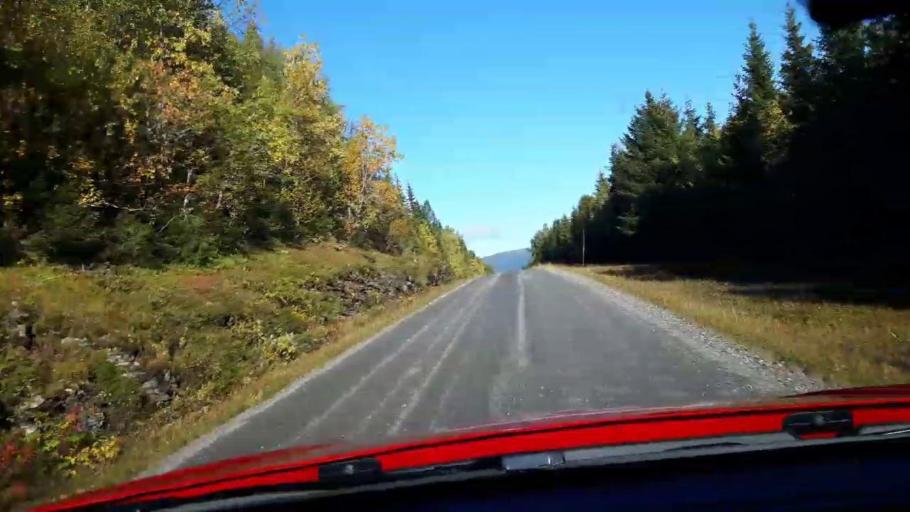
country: NO
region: Nord-Trondelag
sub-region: Lierne
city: Sandvika
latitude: 64.5805
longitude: 13.8910
